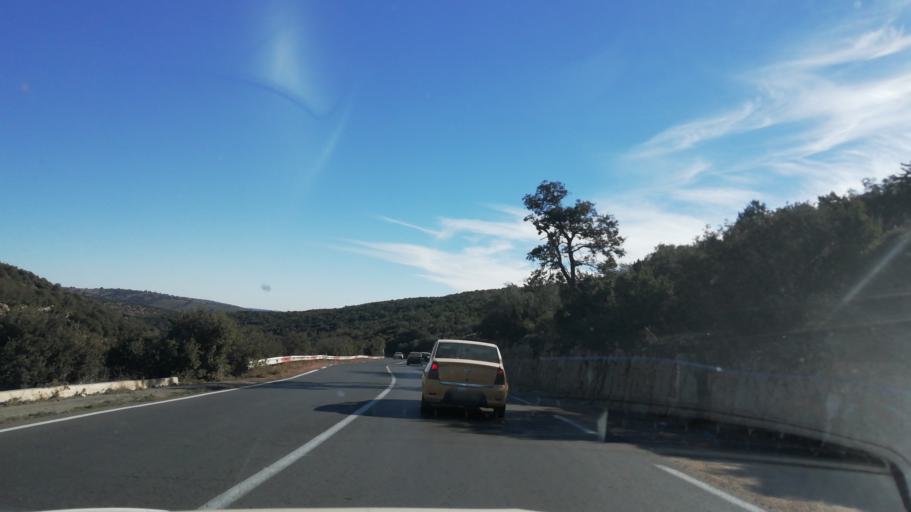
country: DZ
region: Tlemcen
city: Sebdou
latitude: 34.7438
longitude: -1.3493
